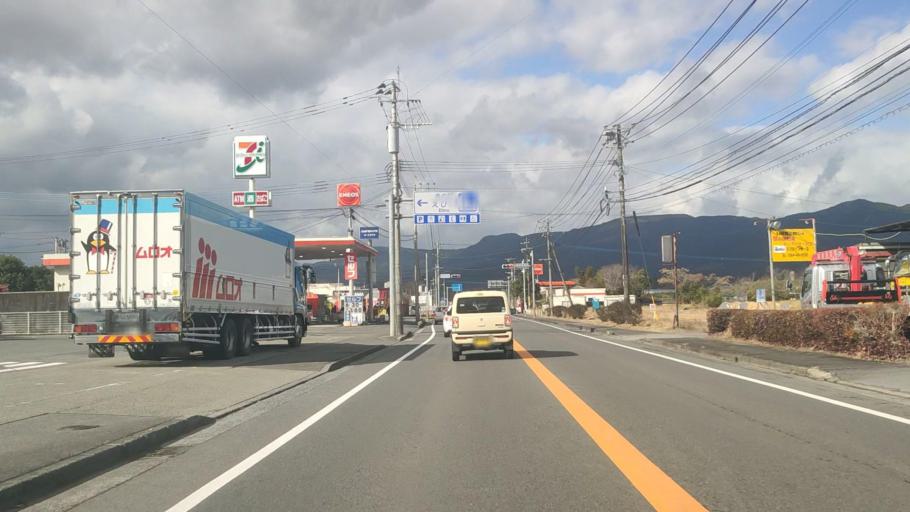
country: JP
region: Kumamoto
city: Hitoyoshi
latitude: 32.0505
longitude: 130.8068
